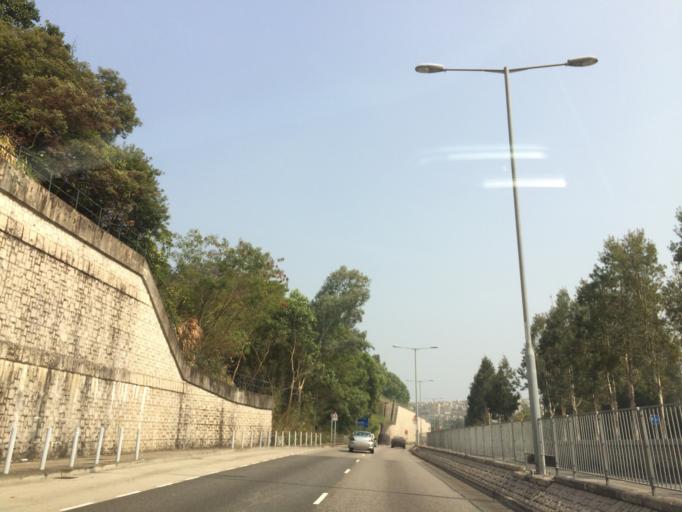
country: HK
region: Tai Po
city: Tai Po
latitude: 22.4596
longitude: 114.2000
